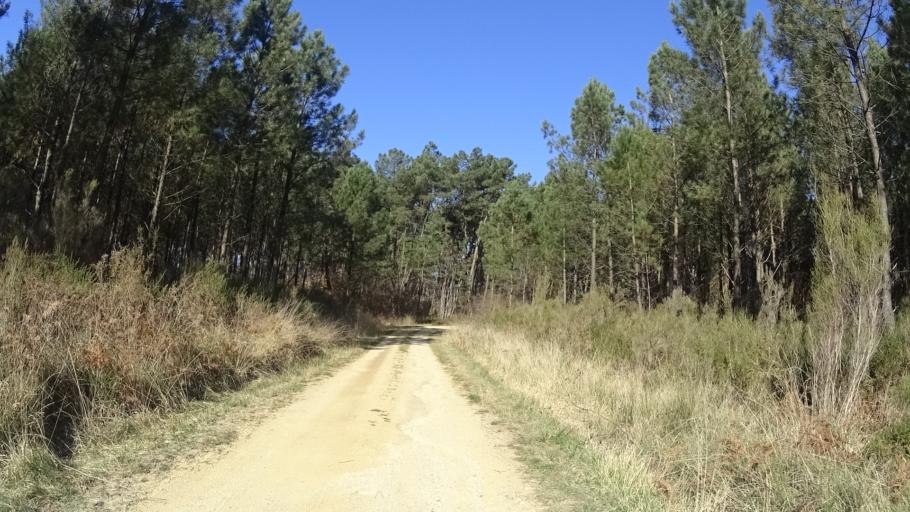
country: FR
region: Aquitaine
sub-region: Departement de la Dordogne
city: Montpon-Menesterol
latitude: 45.0518
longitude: 0.2409
